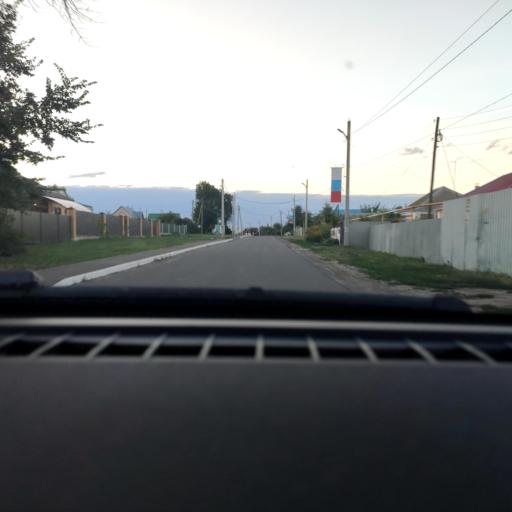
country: RU
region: Voronezj
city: Novaya Usman'
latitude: 51.6624
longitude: 39.3425
